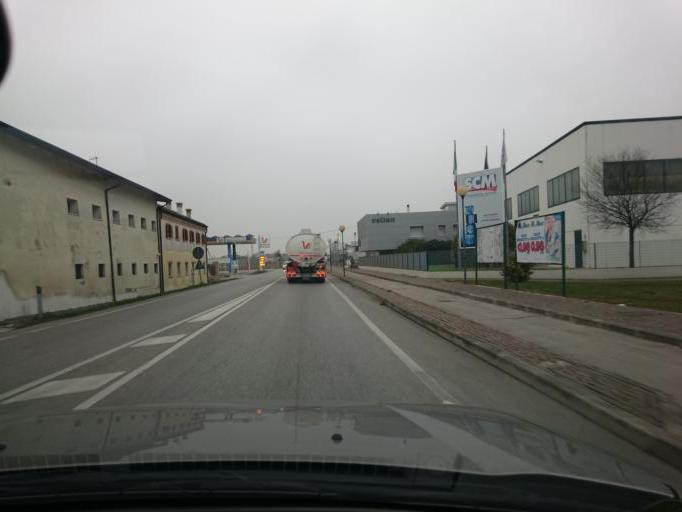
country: IT
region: Veneto
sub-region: Provincia di Padova
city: Sant'Angelo di Piove di Sacco
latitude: 45.3173
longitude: 12.0055
